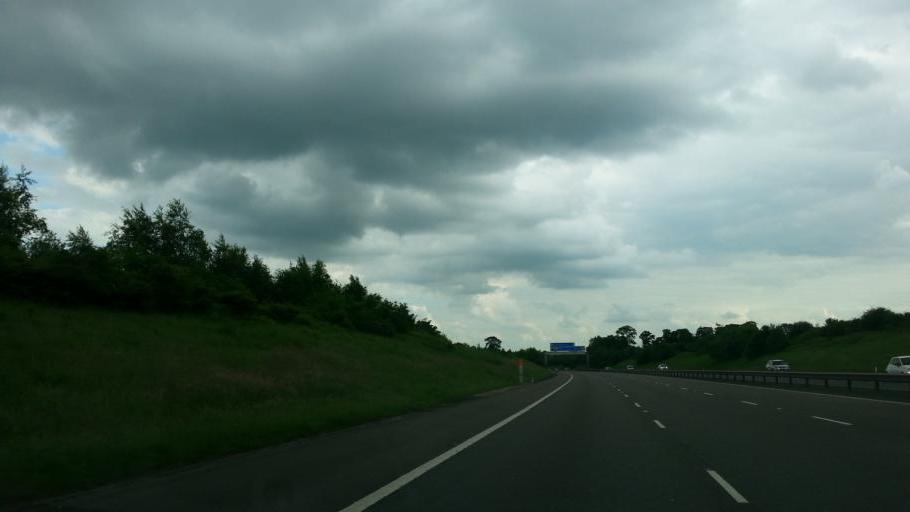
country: GB
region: England
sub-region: City and Borough of Birmingham
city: Sutton Coldfield
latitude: 52.5923
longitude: -1.7955
